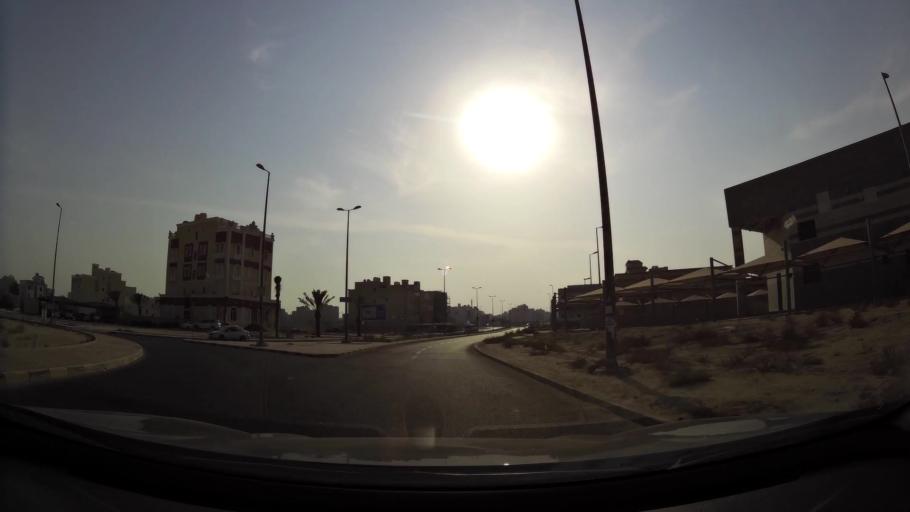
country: KW
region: Mubarak al Kabir
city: Mubarak al Kabir
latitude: 29.1951
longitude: 48.1025
